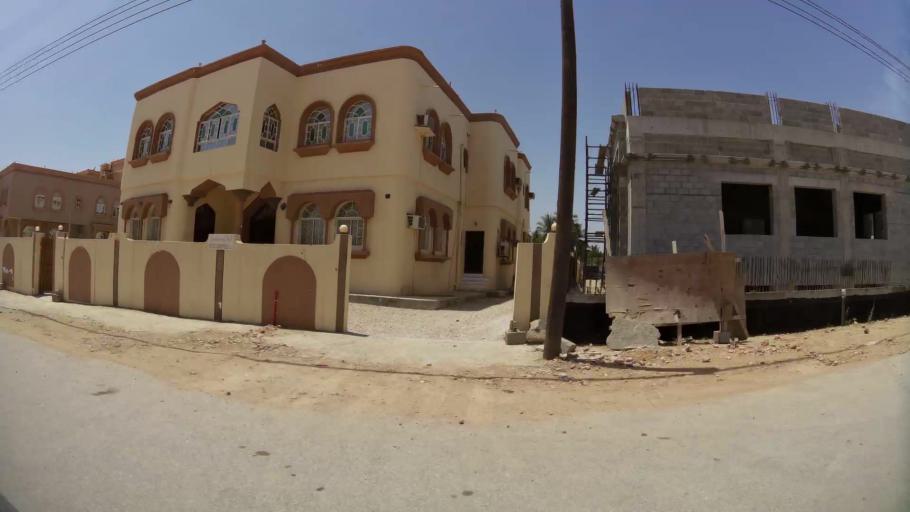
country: OM
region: Zufar
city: Salalah
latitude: 17.0637
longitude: 54.1517
